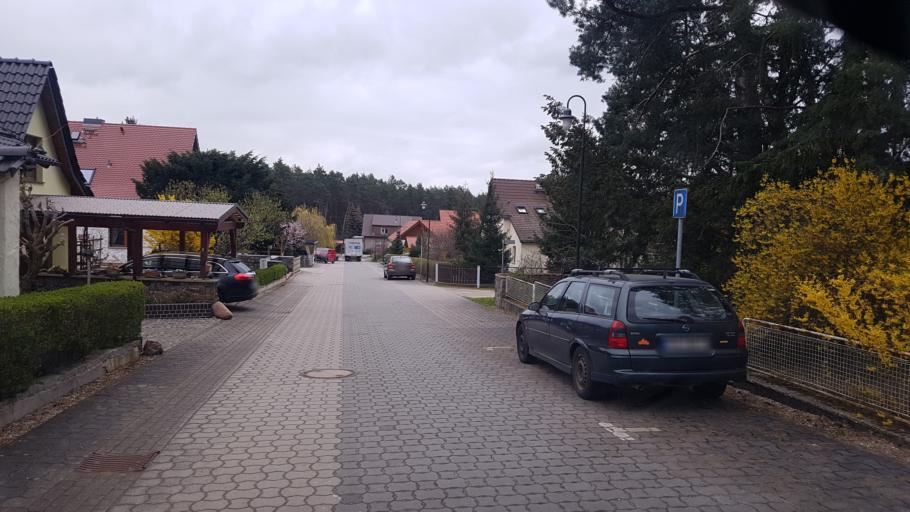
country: DE
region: Brandenburg
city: Senftenberg
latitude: 51.4895
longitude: 14.0642
